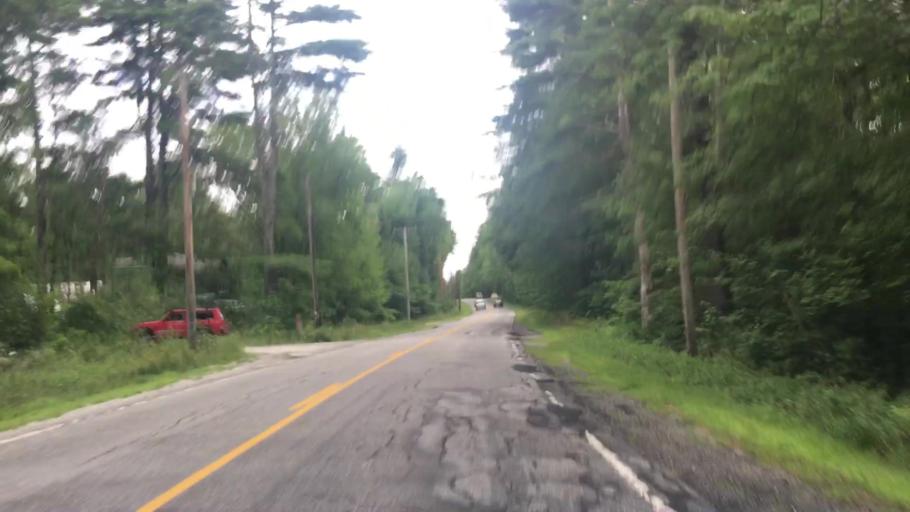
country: US
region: Maine
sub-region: York County
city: Lake Arrowhead
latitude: 43.6611
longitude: -70.7668
